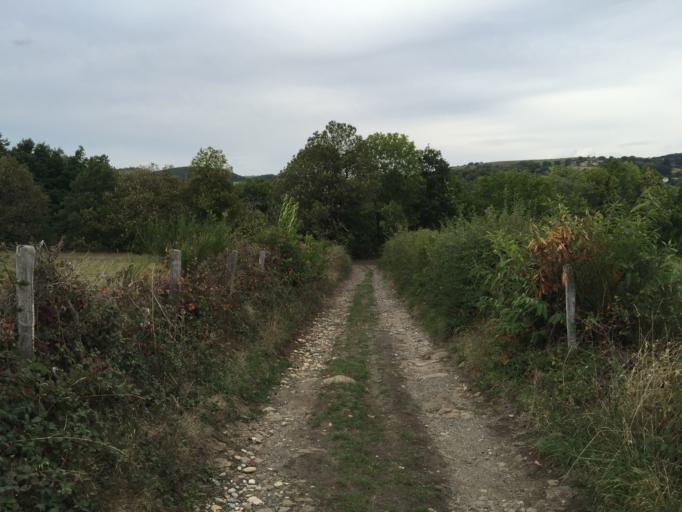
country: FR
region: Rhone-Alpes
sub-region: Departement de la Loire
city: Sorbiers
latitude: 45.4921
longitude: 4.4717
